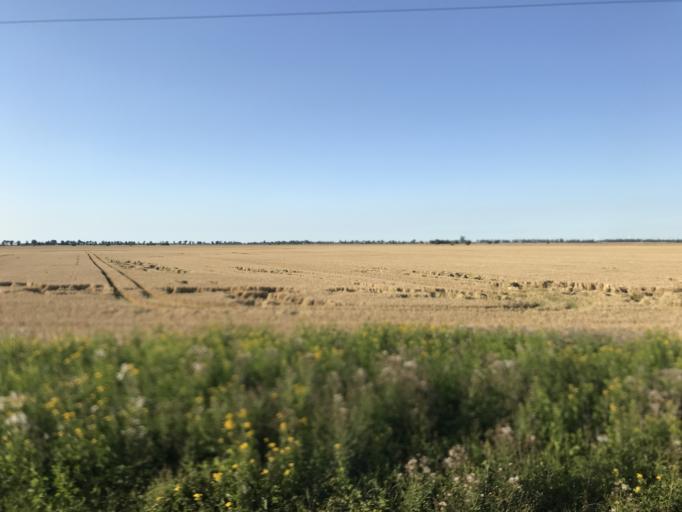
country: PL
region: Pomeranian Voivodeship
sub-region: Powiat malborski
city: Lisewo Malborskie
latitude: 54.0883
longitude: 18.8535
